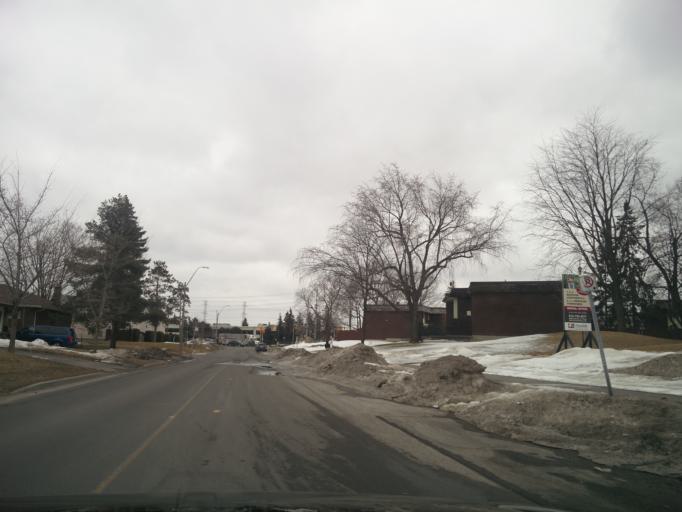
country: CA
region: Ontario
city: Ottawa
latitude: 45.3885
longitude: -75.6227
